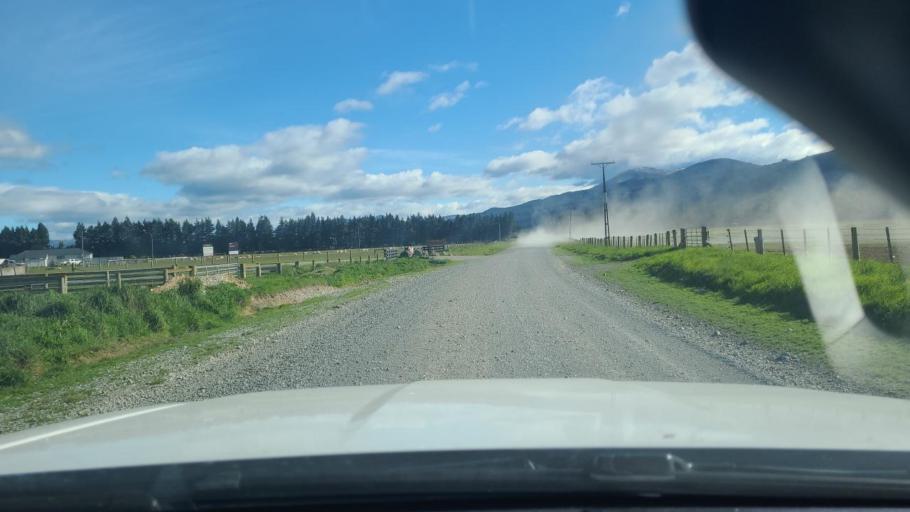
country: NZ
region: Southland
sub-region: Southland District
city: Te Anau
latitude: -45.5375
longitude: 168.1175
